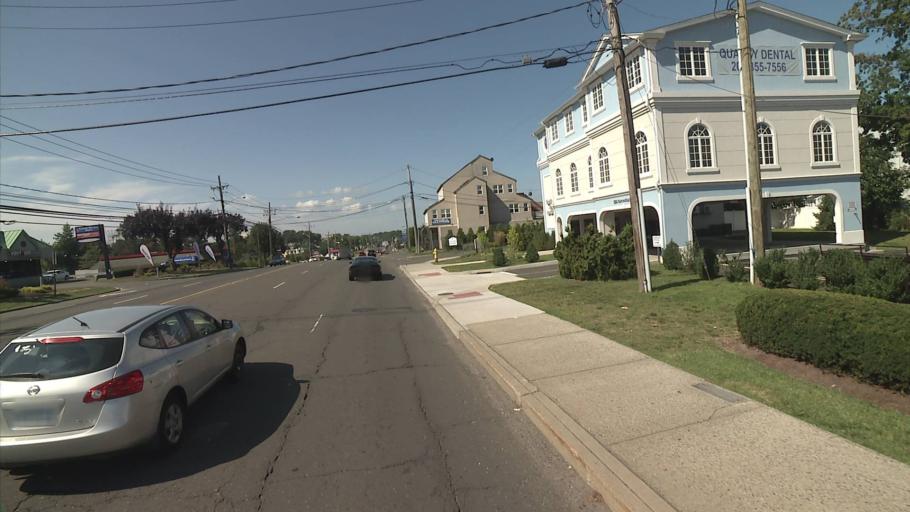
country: US
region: Connecticut
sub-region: Fairfield County
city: Darien
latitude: 41.0975
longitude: -73.4451
